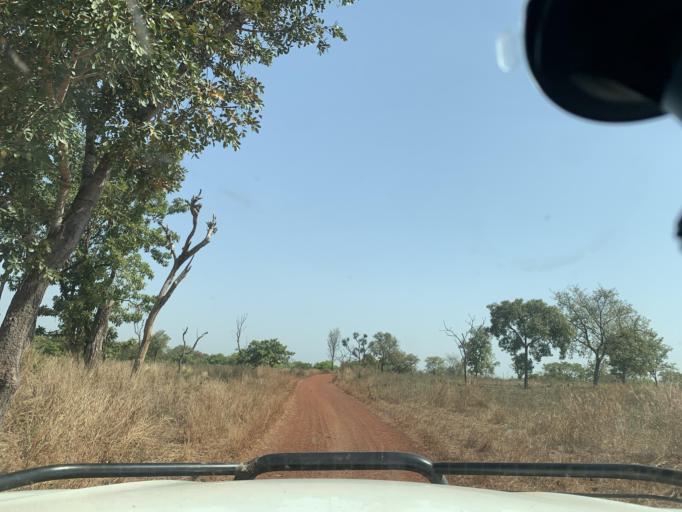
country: ML
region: Sikasso
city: Kolondieba
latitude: 10.8908
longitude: -6.7562
